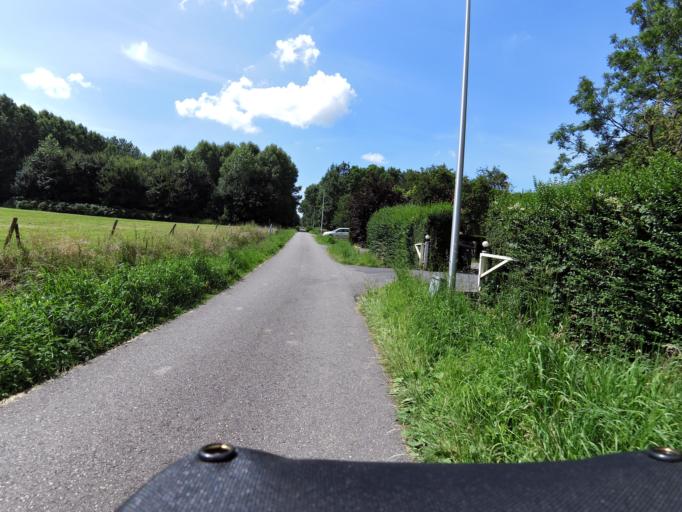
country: NL
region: South Holland
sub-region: Gemeente Albrandswaard
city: Rhoon
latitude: 51.8701
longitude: 4.4106
